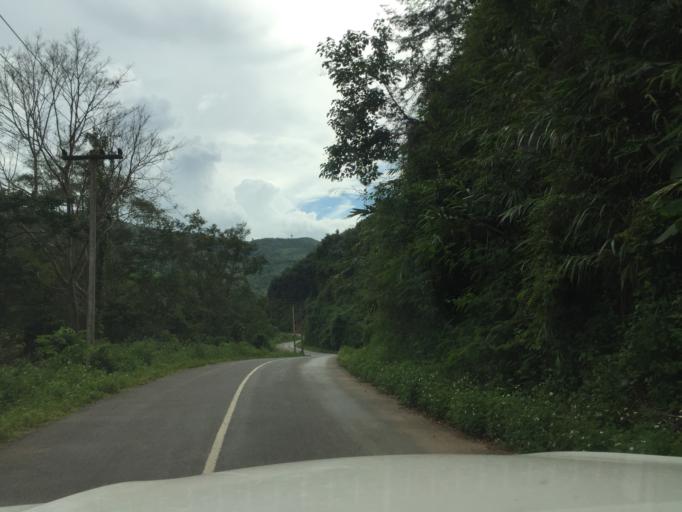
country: LA
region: Oudomxai
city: Muang La
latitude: 21.1066
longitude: 102.2310
